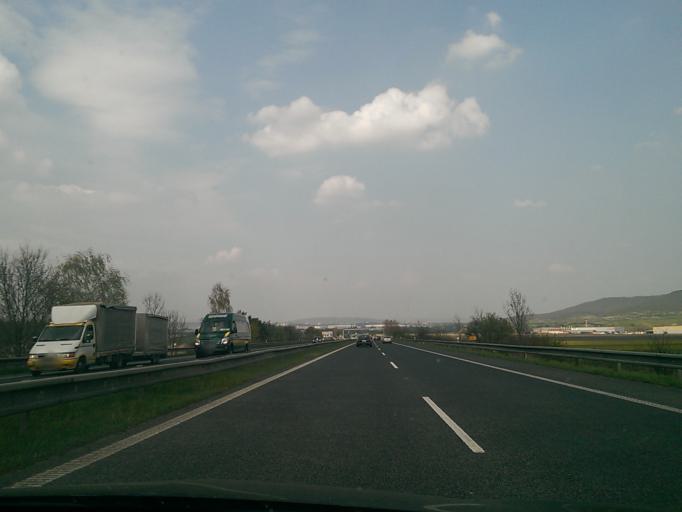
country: CZ
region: Central Bohemia
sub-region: Okres Mlada Boleslav
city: Mlada Boleslav
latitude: 50.3692
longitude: 14.8813
